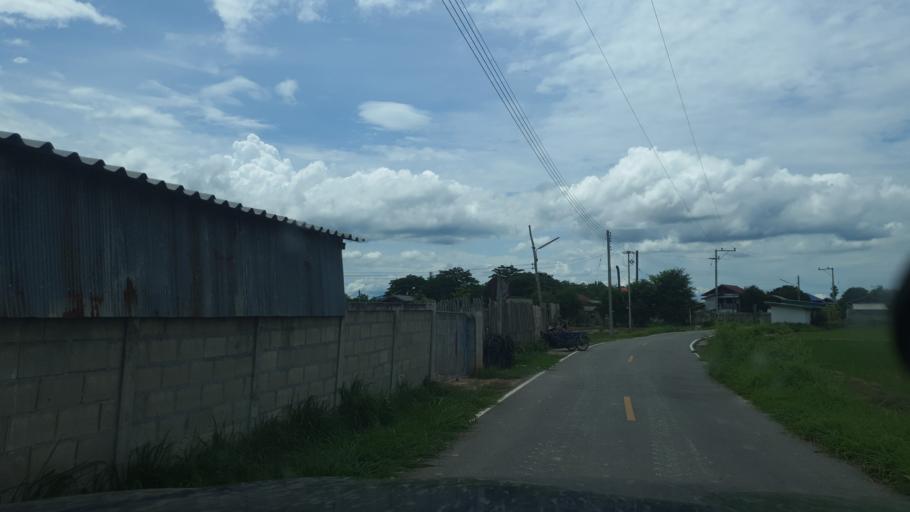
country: TH
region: Lampang
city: Sop Prap
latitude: 17.8761
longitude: 99.3840
